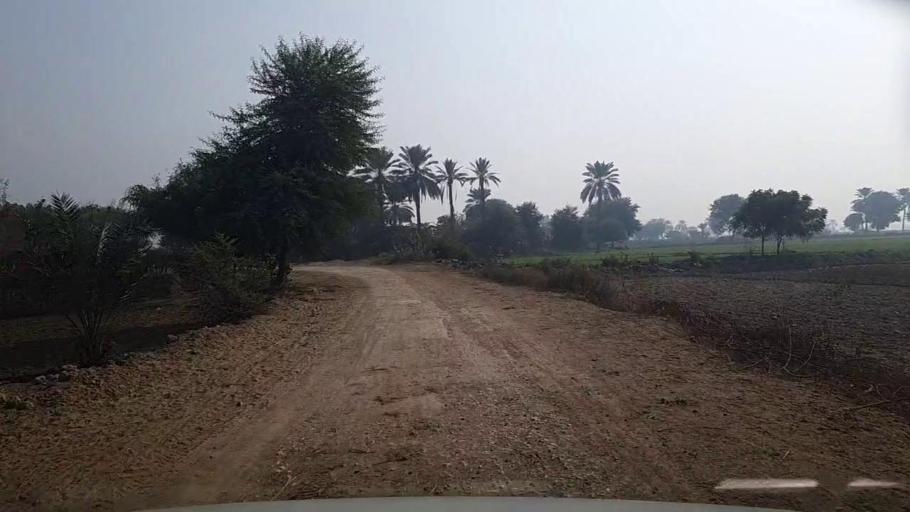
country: PK
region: Sindh
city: Setharja Old
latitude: 27.1418
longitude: 68.4945
